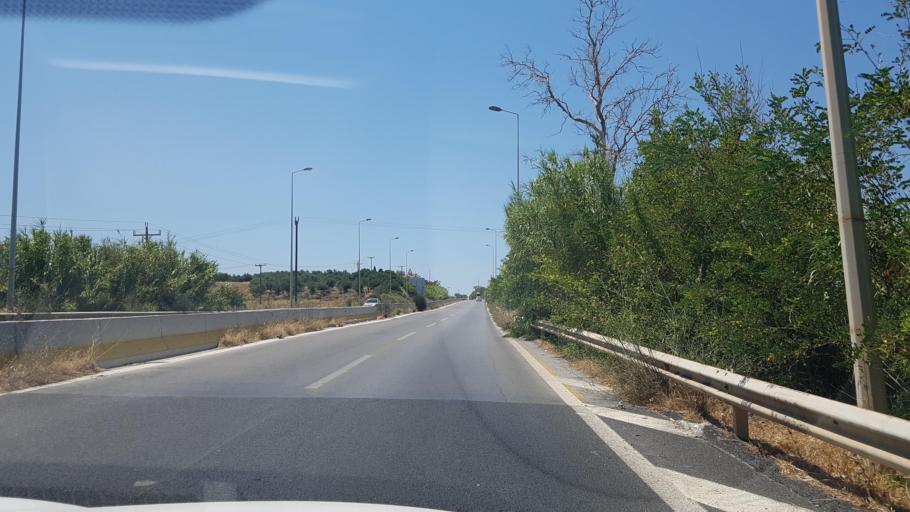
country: GR
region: Crete
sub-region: Nomos Rethymnis
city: Rethymno
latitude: 35.3636
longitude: 24.5087
